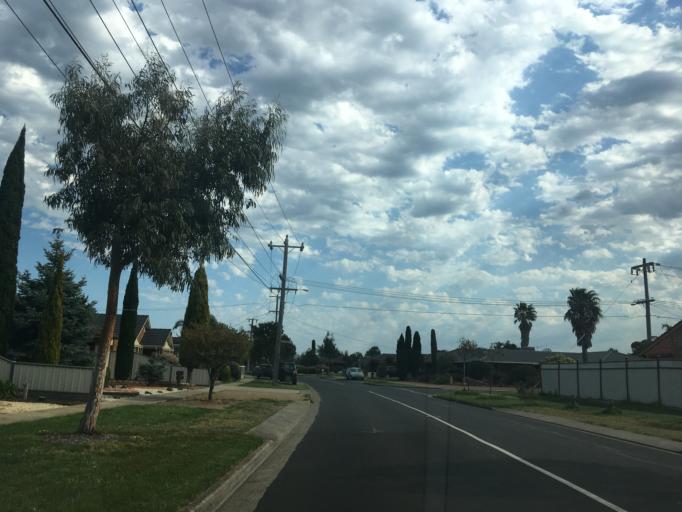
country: AU
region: Victoria
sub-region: Wyndham
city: Hoppers Crossing
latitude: -37.8632
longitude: 144.7101
